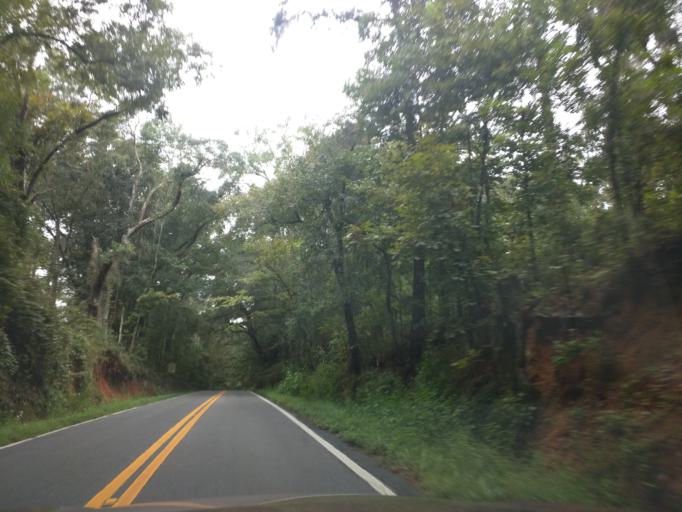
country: US
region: Florida
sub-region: Leon County
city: Tallahassee
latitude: 30.4824
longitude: -84.2030
